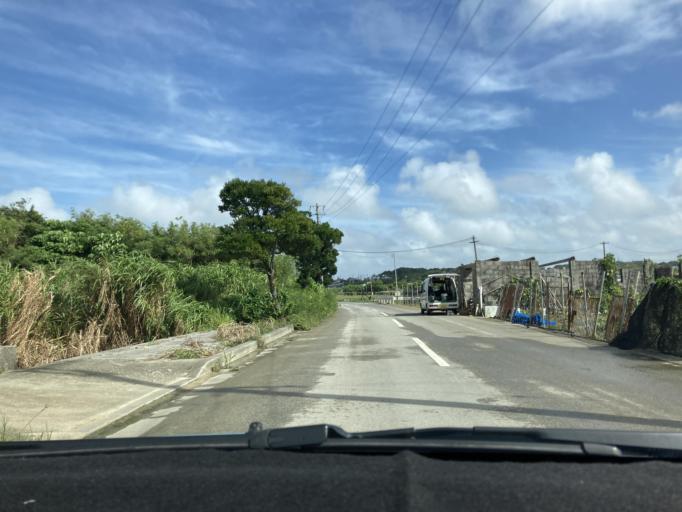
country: JP
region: Okinawa
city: Itoman
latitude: 26.0990
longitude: 127.6612
